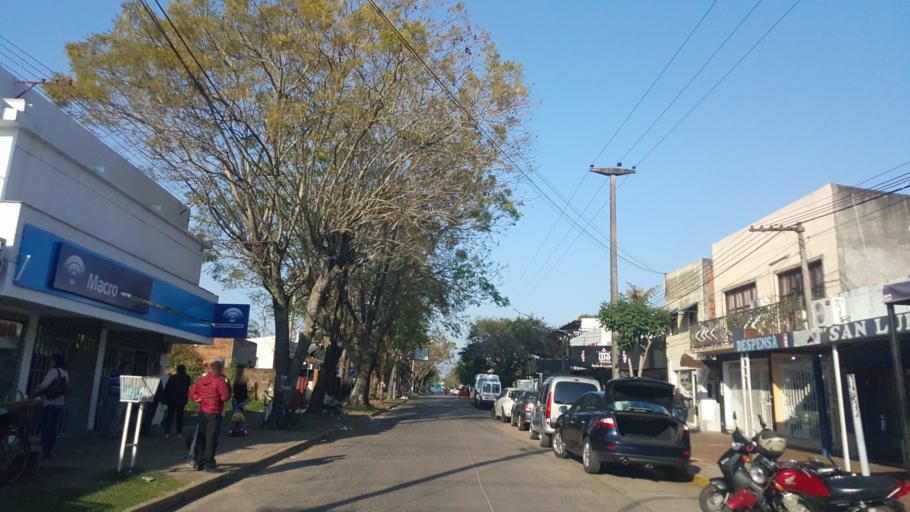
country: AR
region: Corrientes
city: Ituzaingo
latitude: -27.5825
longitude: -56.6850
